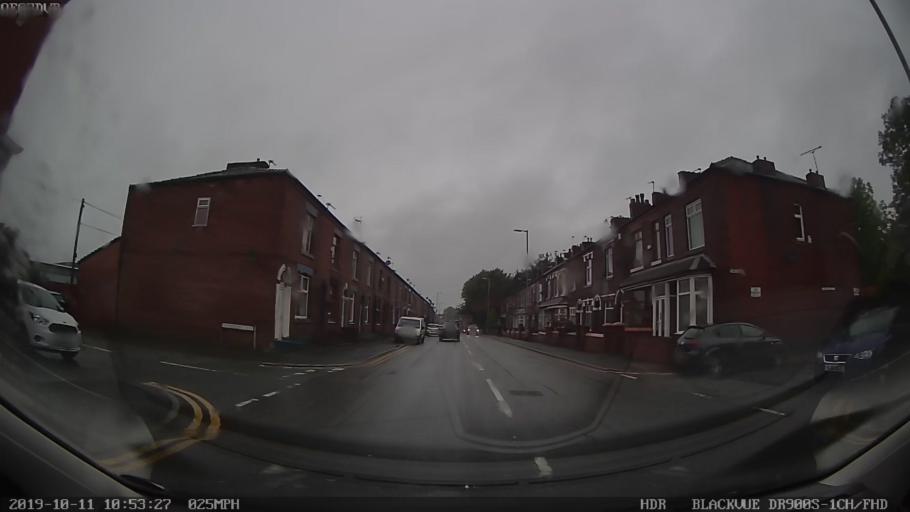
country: GB
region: England
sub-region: Borough of Oldham
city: Oldham
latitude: 53.5471
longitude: -2.1502
